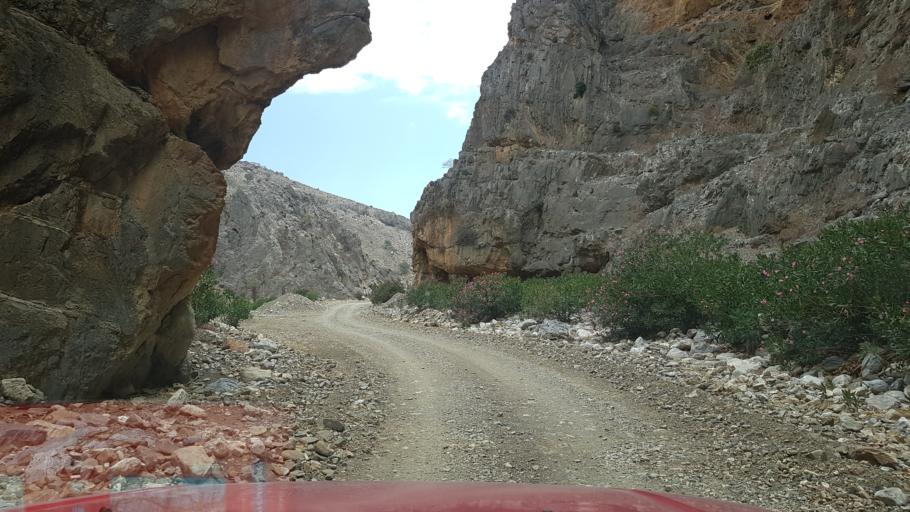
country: GR
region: Crete
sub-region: Nomos Irakleiou
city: Agioi Deka
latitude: 34.9420
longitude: 24.9841
